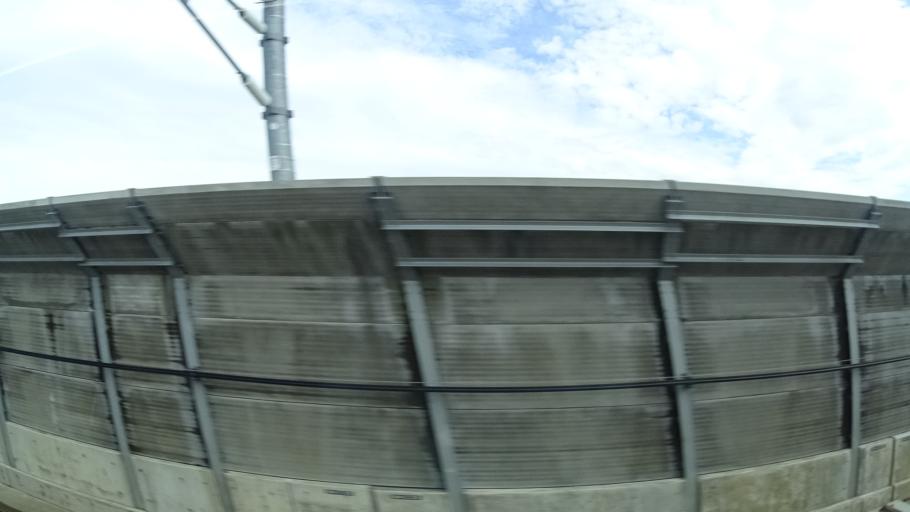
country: JP
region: Toyama
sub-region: Oyabe Shi
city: Oyabe
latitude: 36.6816
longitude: 136.9103
